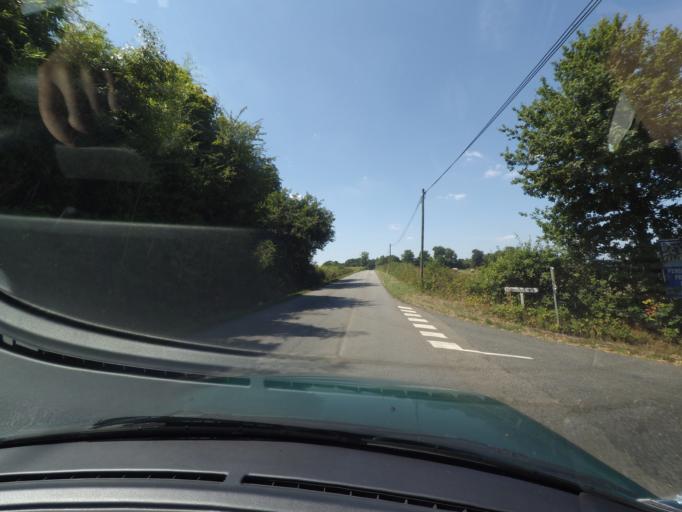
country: FR
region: Limousin
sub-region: Departement de la Haute-Vienne
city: Aixe-sur-Vienne
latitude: 45.7841
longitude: 1.1581
